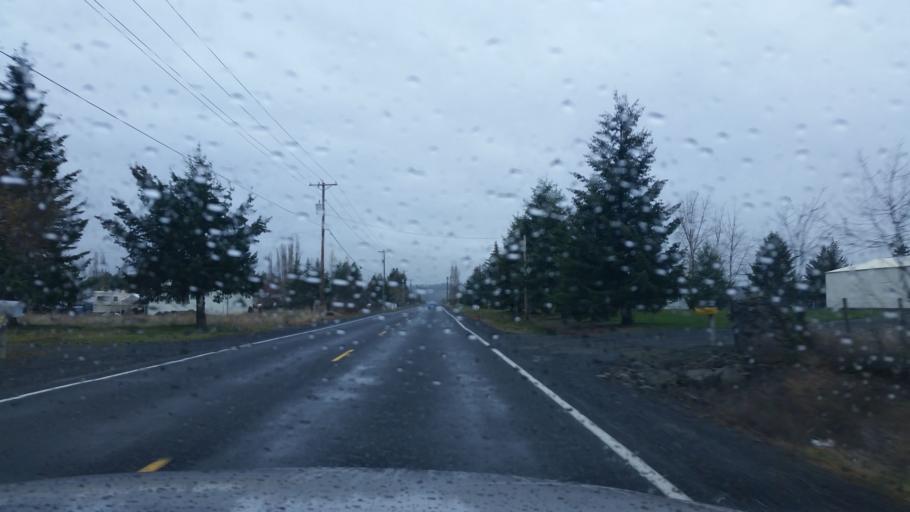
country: US
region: Washington
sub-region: Spokane County
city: Fairchild Air Force Base
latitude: 47.5913
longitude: -117.6076
